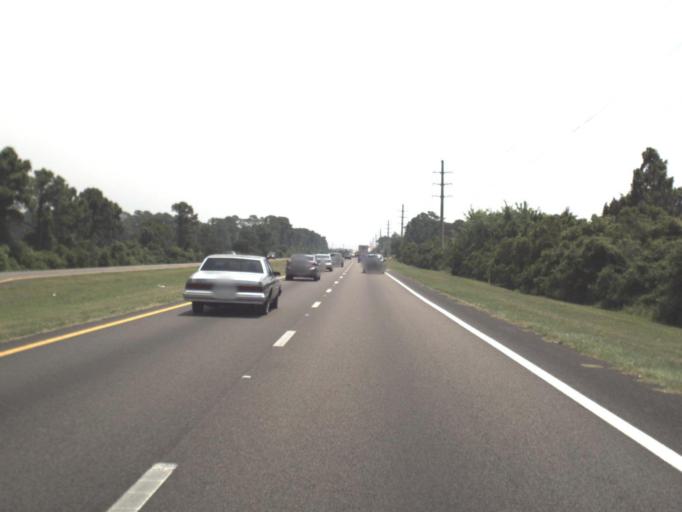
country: US
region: Florida
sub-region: Nassau County
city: Fernandina Beach
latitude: 30.6174
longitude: -81.5047
